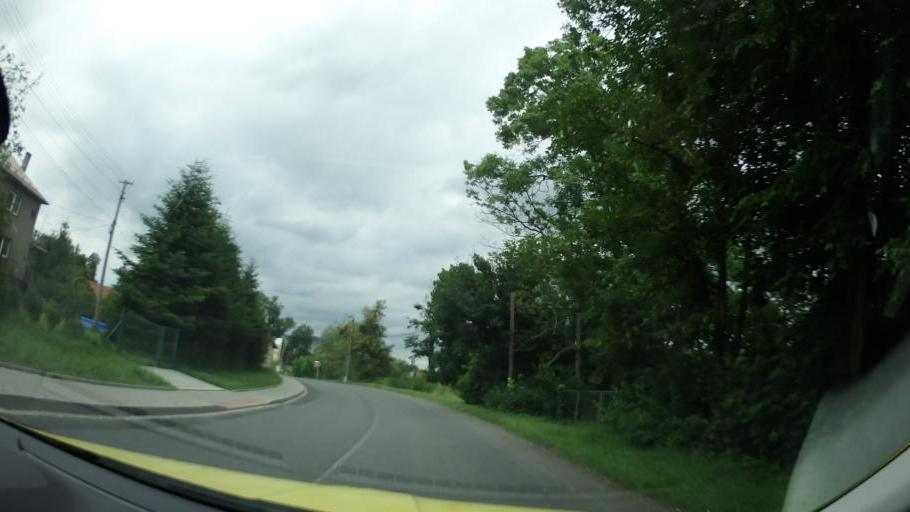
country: CZ
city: Verovice
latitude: 49.5608
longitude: 18.1062
